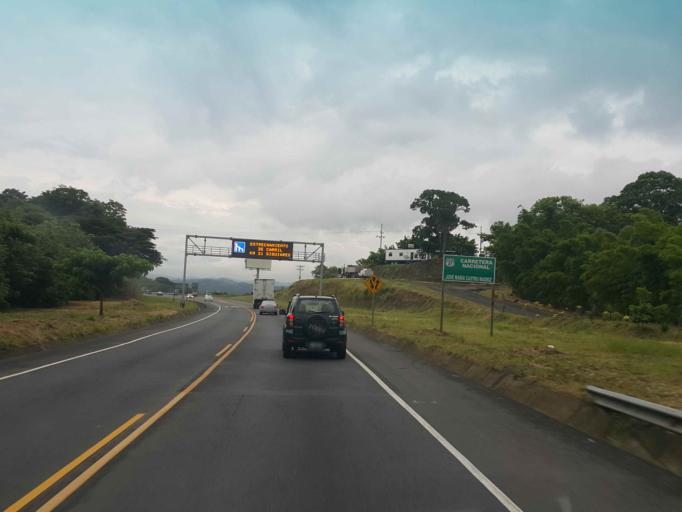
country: CR
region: Alajuela
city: Atenas
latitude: 9.9497
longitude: -84.3620
